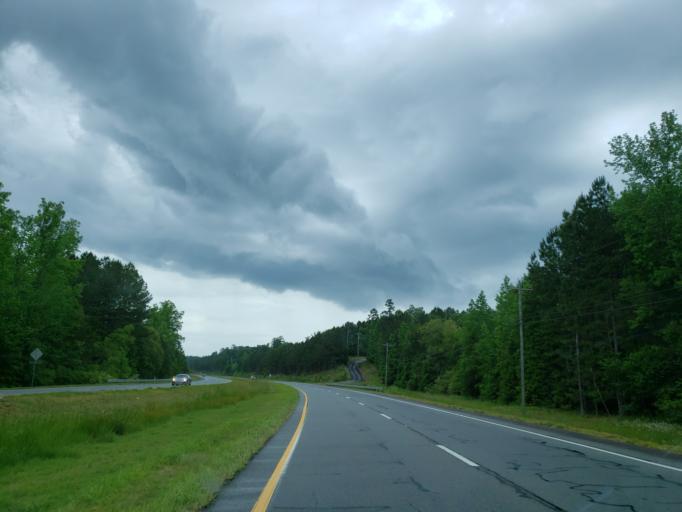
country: US
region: Georgia
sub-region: Haralson County
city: Buchanan
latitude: 33.8543
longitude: -85.2100
